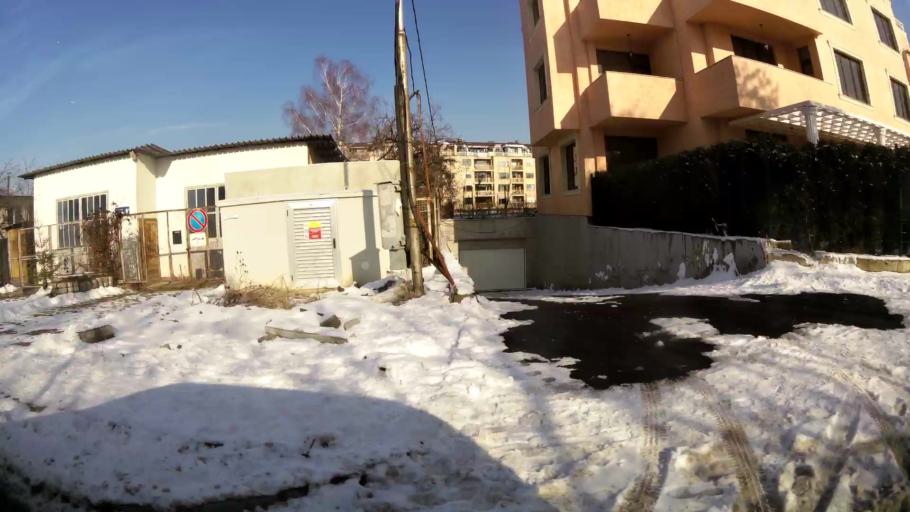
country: BG
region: Sofia-Capital
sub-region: Stolichna Obshtina
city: Sofia
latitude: 42.6542
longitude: 23.3310
